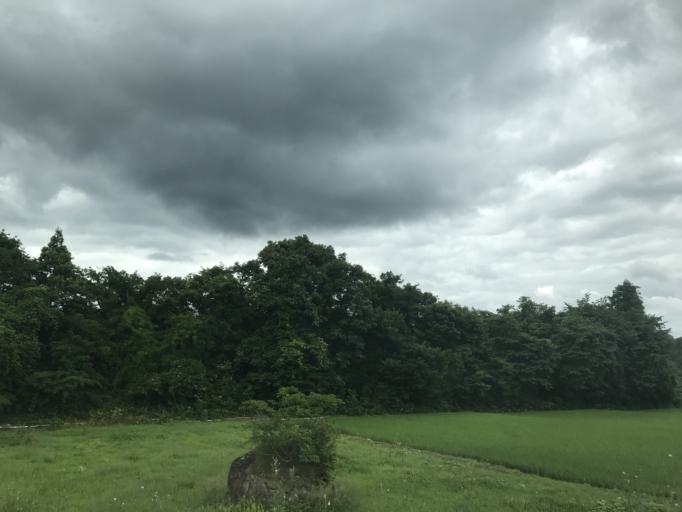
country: JP
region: Iwate
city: Ichinoseki
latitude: 38.9705
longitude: 140.9322
